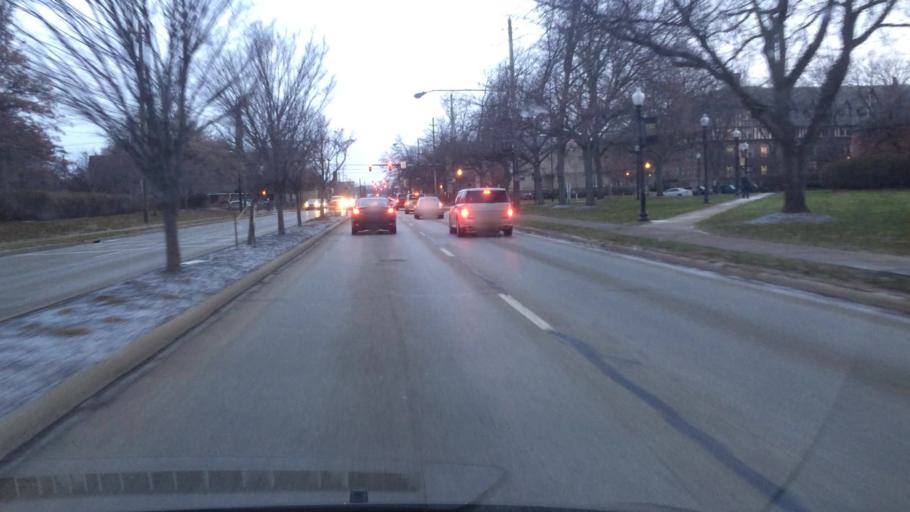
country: US
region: Ohio
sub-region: Cuyahoga County
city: Berea
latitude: 41.3726
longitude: -81.8486
